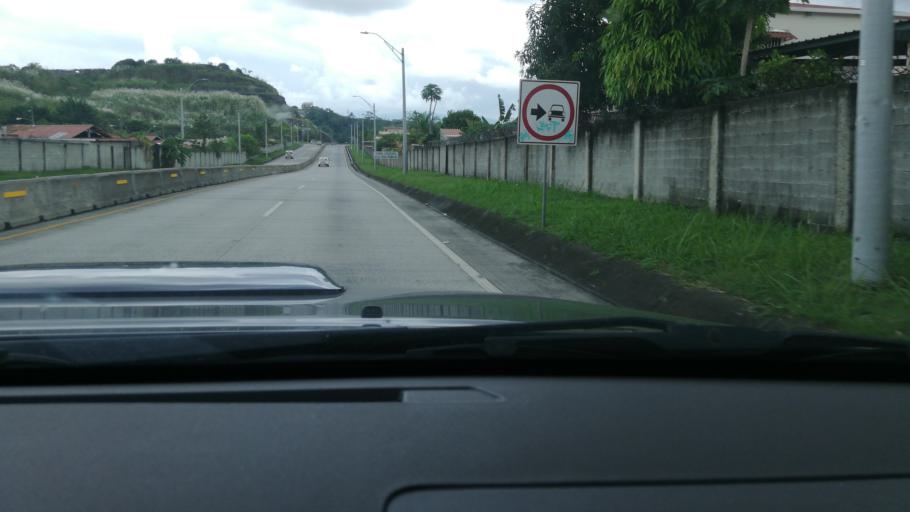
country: PA
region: Panama
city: San Miguelito
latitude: 9.0544
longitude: -79.4832
